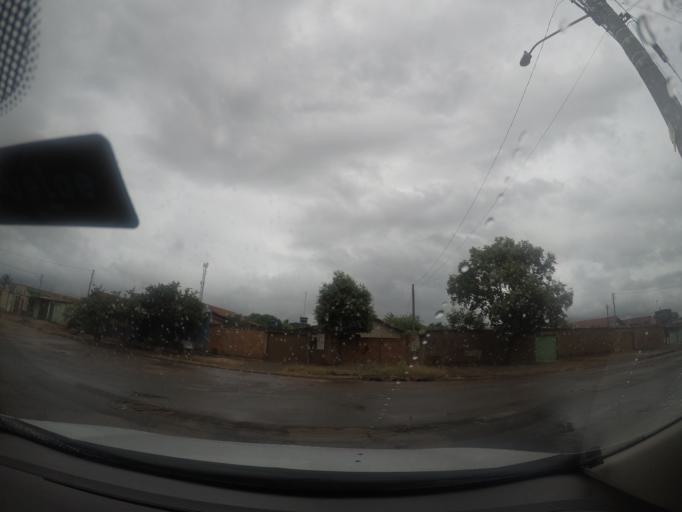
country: BR
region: Goias
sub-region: Trindade
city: Trindade
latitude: -16.6452
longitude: -49.3870
